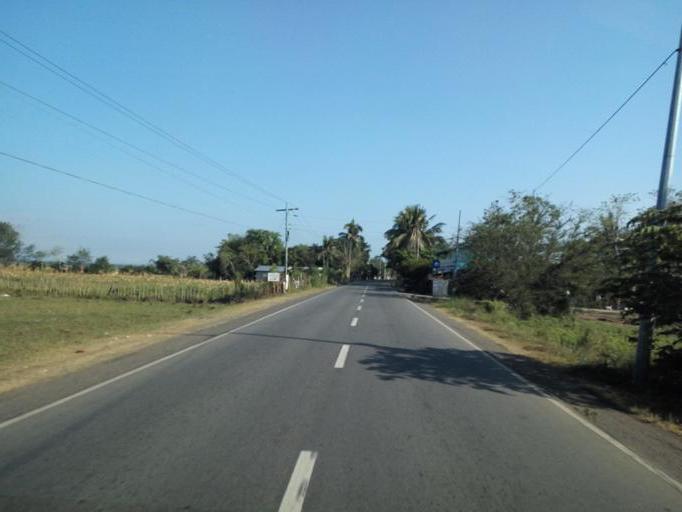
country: PH
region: Cagayan Valley
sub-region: Province of Cagayan
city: Amulung
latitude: 17.8272
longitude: 121.7250
